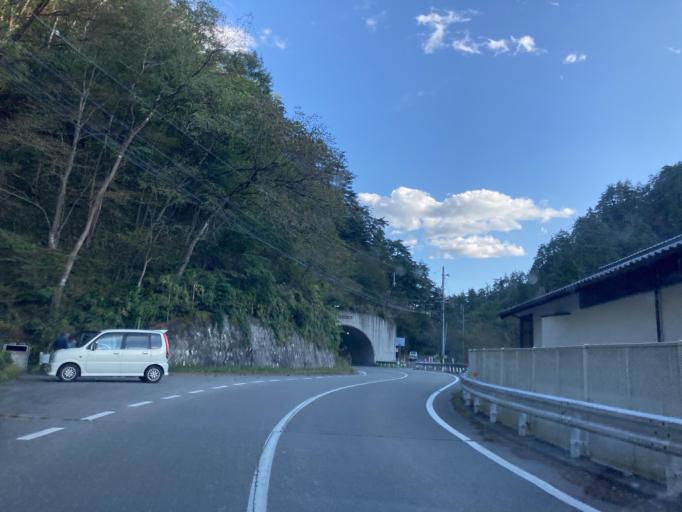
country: JP
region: Nagano
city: Omachi
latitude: 36.4513
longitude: 137.9783
